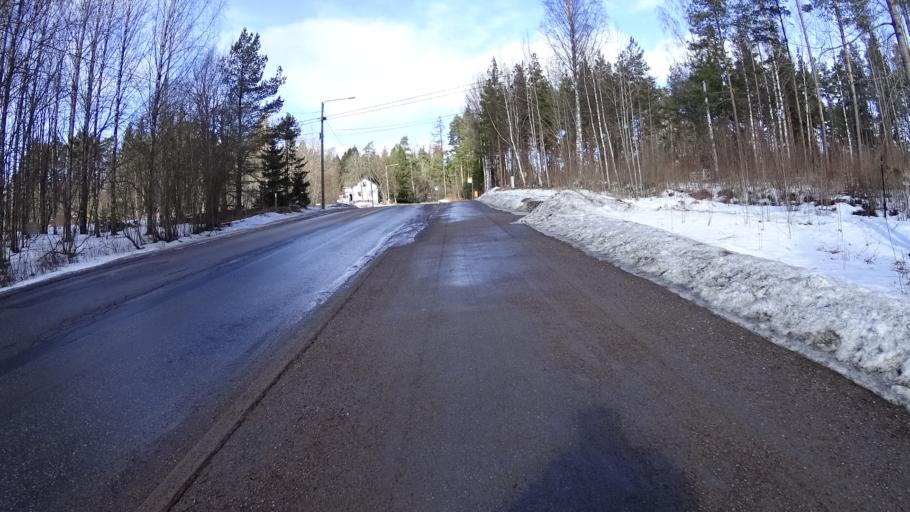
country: FI
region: Uusimaa
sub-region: Helsinki
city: Espoo
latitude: 60.2435
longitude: 24.6548
